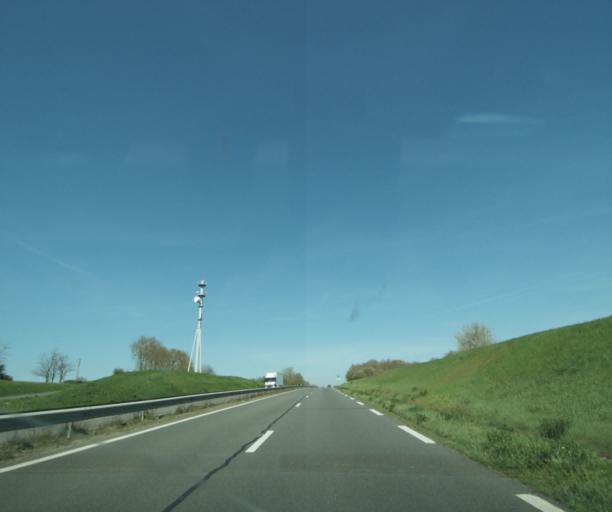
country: FR
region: Bourgogne
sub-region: Departement de la Nievre
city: Saint-Pierre-le-Moutier
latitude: 46.7793
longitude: 3.1296
